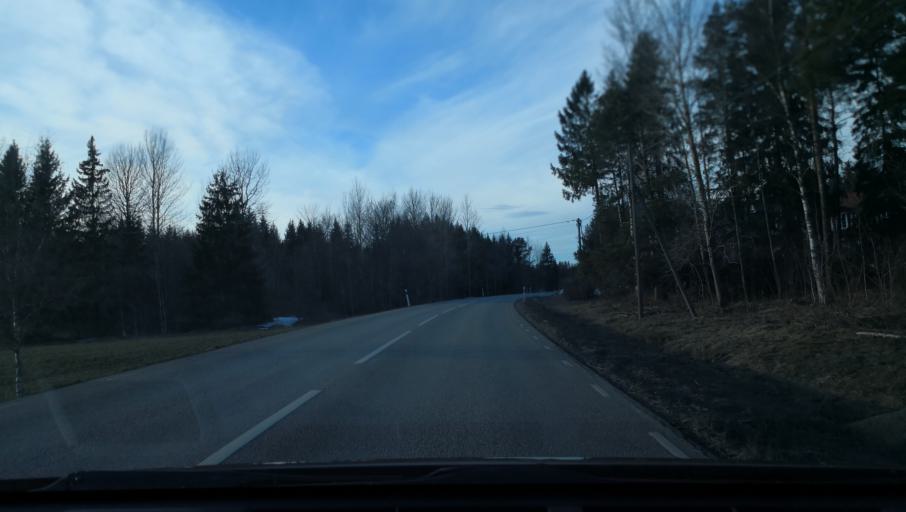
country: SE
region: Uppsala
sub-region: Osthammars Kommun
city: OEsthammar
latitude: 60.2999
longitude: 18.2787
